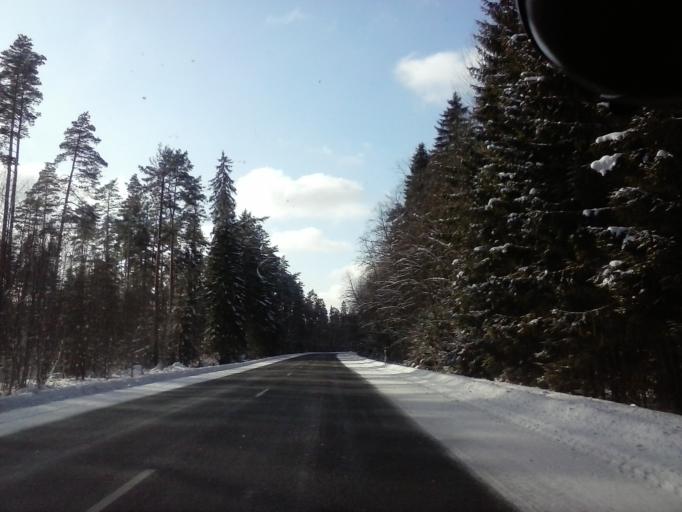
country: EE
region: Viljandimaa
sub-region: Moisakuela linn
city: Moisakula
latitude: 58.2533
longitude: 25.1975
